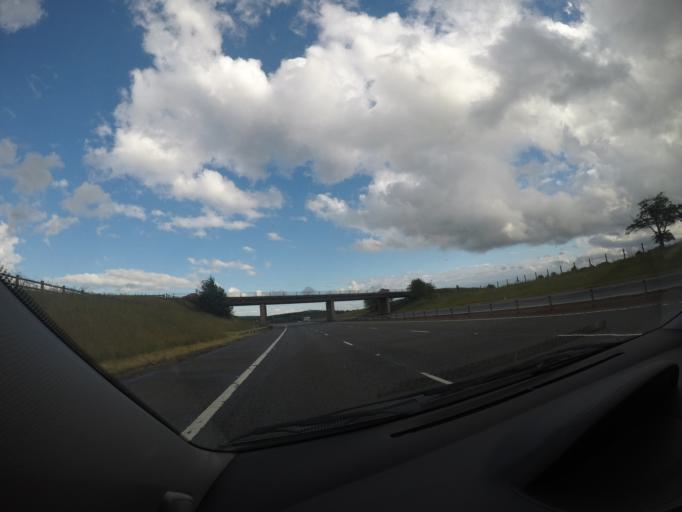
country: GB
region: Scotland
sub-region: Dumfries and Galloway
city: Lockerbie
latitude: 55.1047
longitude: -3.3500
